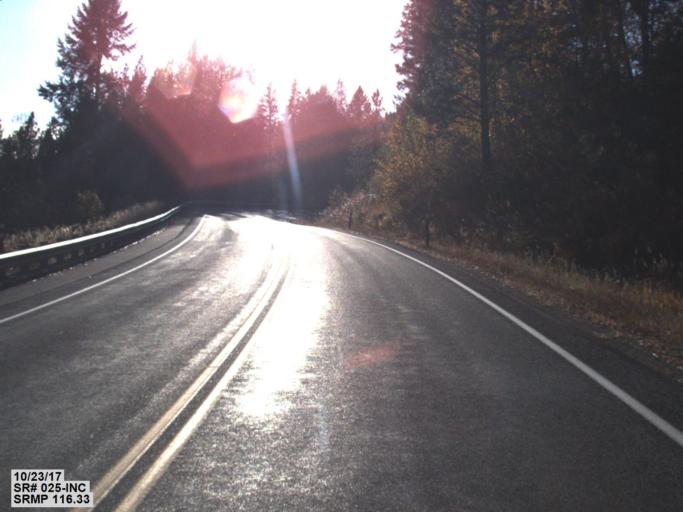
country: CA
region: British Columbia
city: Rossland
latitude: 48.9447
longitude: -117.7844
